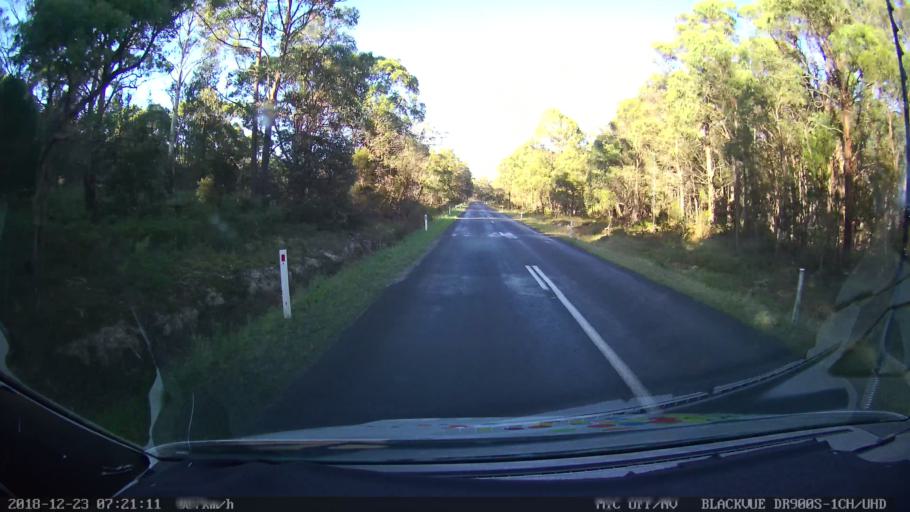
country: AU
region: New South Wales
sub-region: Bellingen
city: Dorrigo
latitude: -30.4960
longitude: 152.2668
